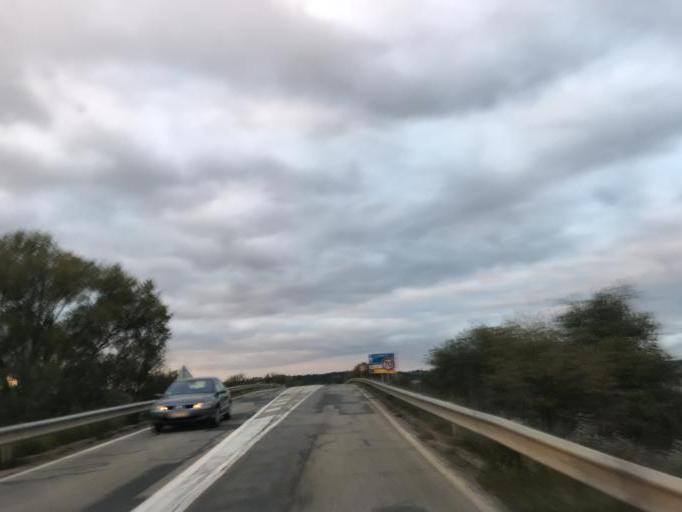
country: FR
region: Rhone-Alpes
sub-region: Departement de l'Ain
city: Trevoux
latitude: 45.9239
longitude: 4.7591
